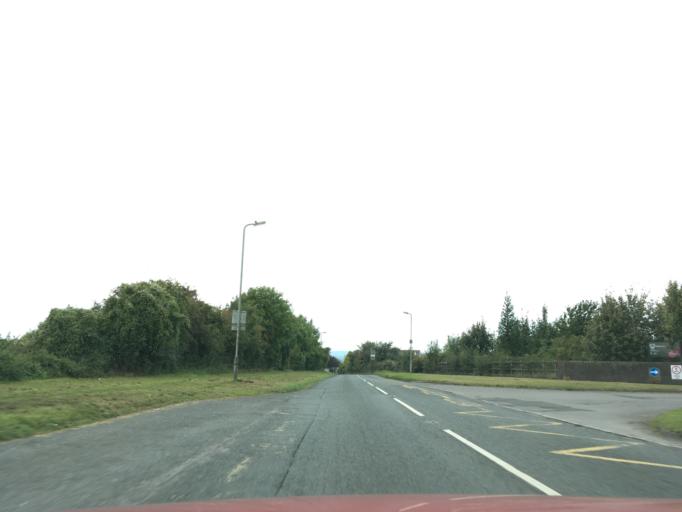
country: GB
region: England
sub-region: South Gloucestershire
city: Alveston
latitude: 51.5930
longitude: -2.5404
